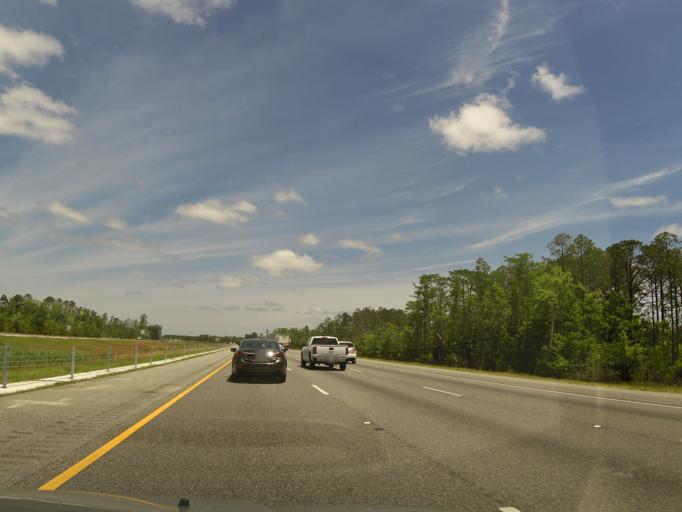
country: US
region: Georgia
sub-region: McIntosh County
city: Darien
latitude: 31.4110
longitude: -81.4445
